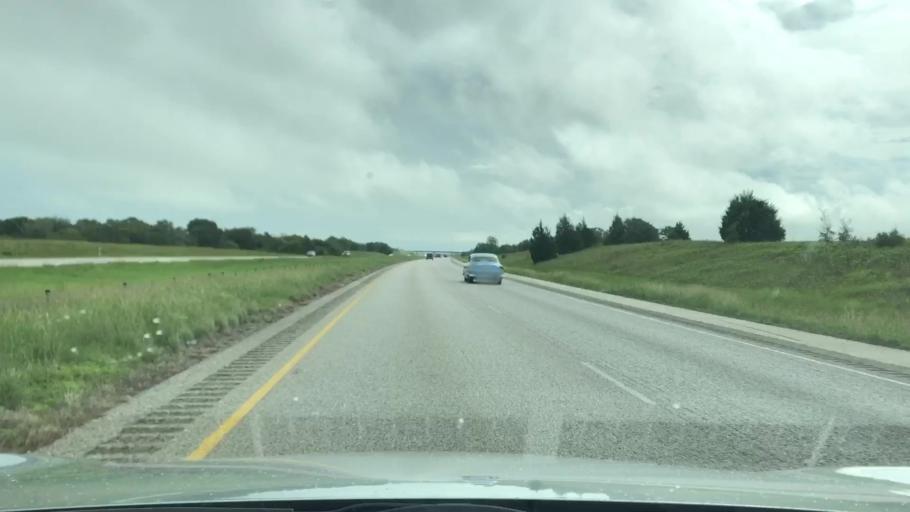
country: US
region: Texas
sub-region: Fayette County
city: Schulenburg
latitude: 29.6910
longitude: -96.9791
